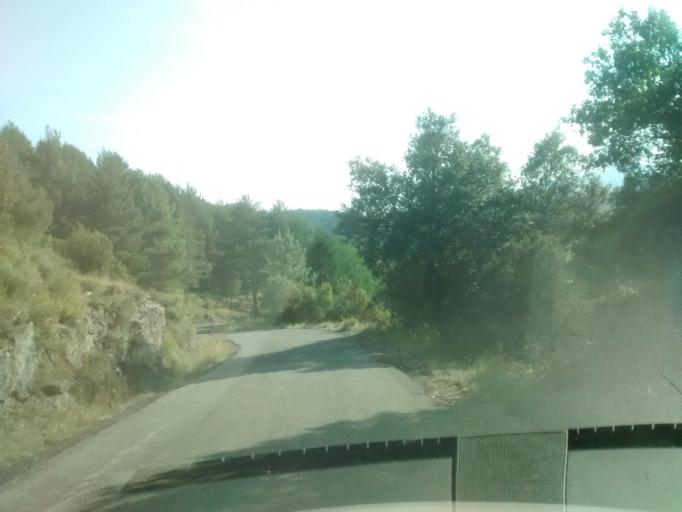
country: ES
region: Aragon
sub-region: Provincia de Huesca
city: Puertolas
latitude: 42.5559
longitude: 0.1692
